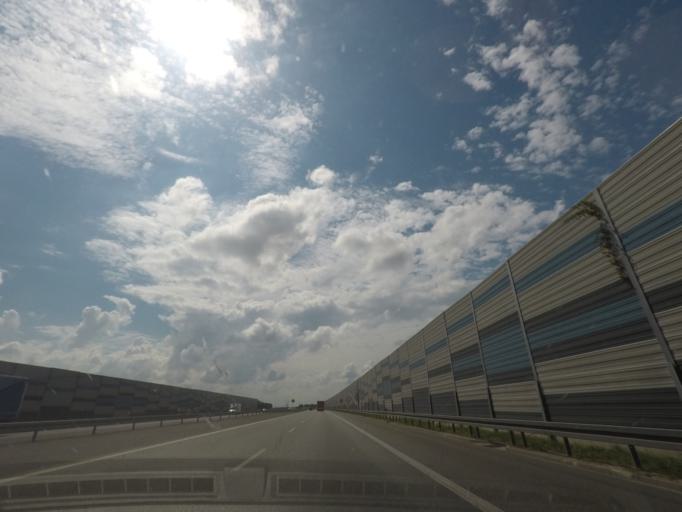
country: PL
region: Lodz Voivodeship
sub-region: Powiat leczycki
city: Piatek
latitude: 52.0158
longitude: 19.5418
